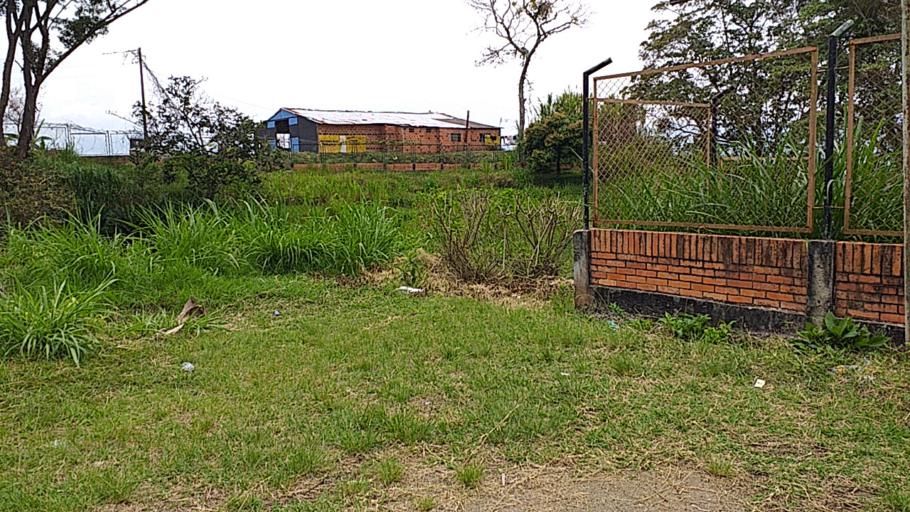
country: CO
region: Boyaca
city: Santana
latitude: 6.0601
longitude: -73.4830
